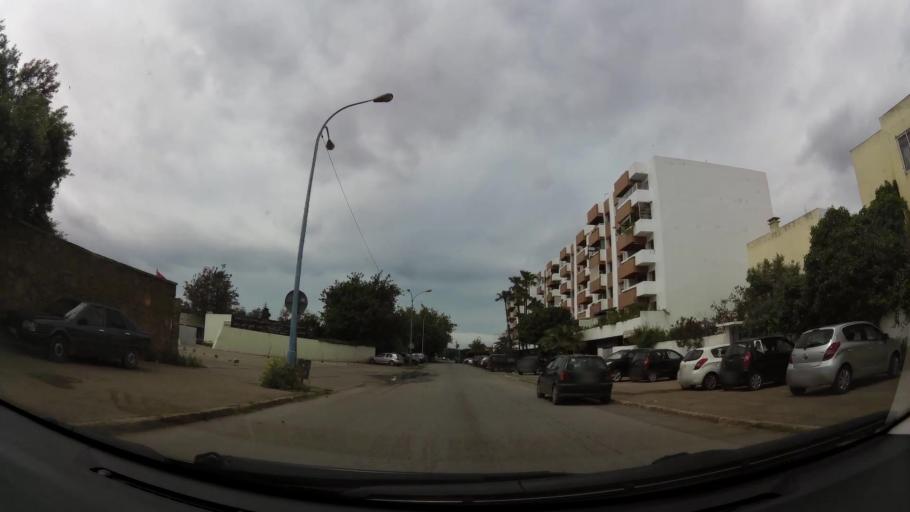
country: MA
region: Grand Casablanca
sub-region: Casablanca
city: Casablanca
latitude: 33.5736
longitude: -7.6515
